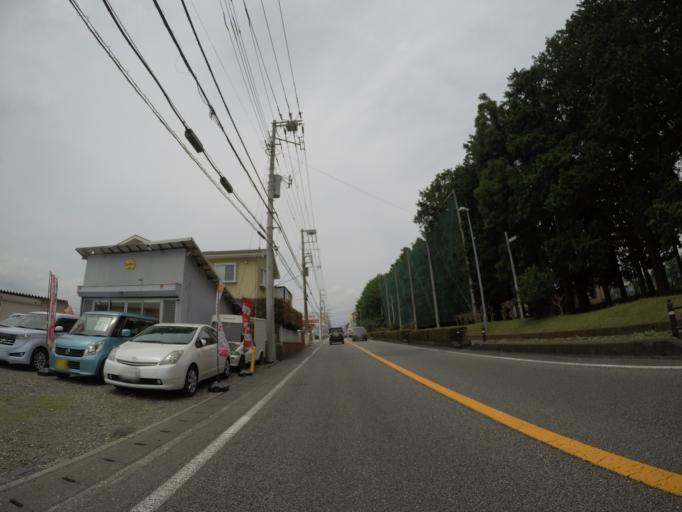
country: JP
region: Shizuoka
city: Fujinomiya
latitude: 35.2380
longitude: 138.6095
